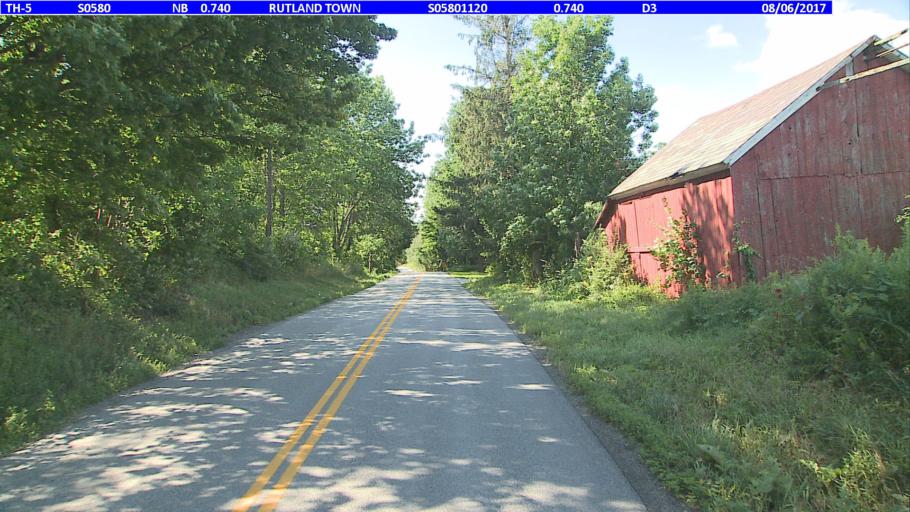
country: US
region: Vermont
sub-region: Rutland County
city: Rutland
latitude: 43.5754
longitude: -72.9515
